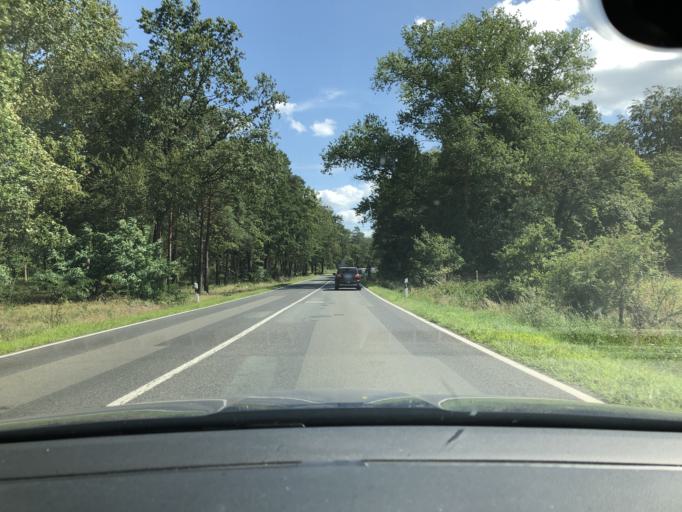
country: DE
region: Brandenburg
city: Lindow
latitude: 52.9257
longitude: 12.9216
